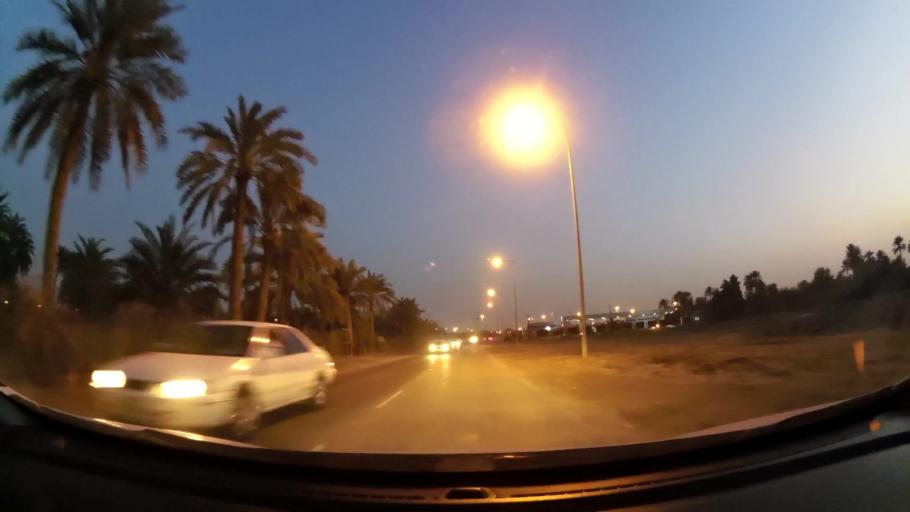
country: BH
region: Manama
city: Jidd Hafs
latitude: 26.2008
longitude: 50.5527
